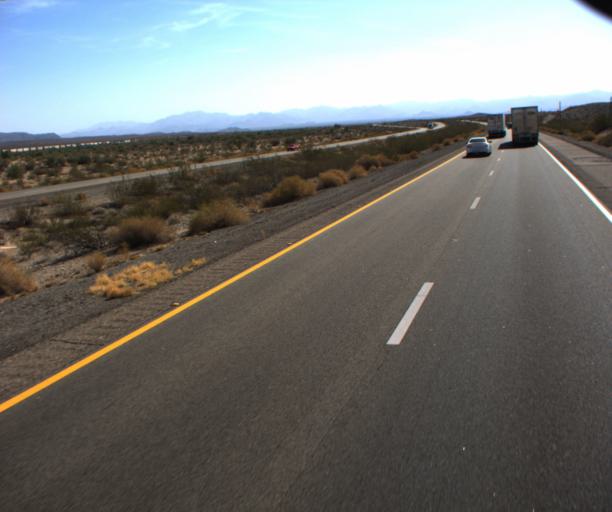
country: US
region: Arizona
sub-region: Mohave County
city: Desert Hills
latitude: 34.7319
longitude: -114.2675
